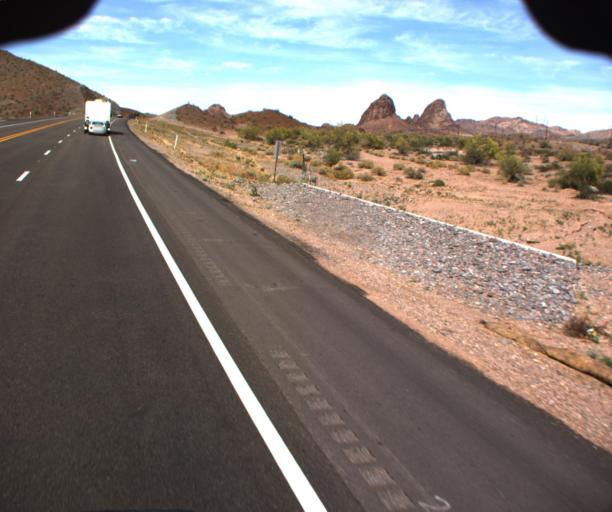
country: US
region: Arizona
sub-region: Mohave County
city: Desert Hills
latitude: 34.5987
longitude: -114.3676
